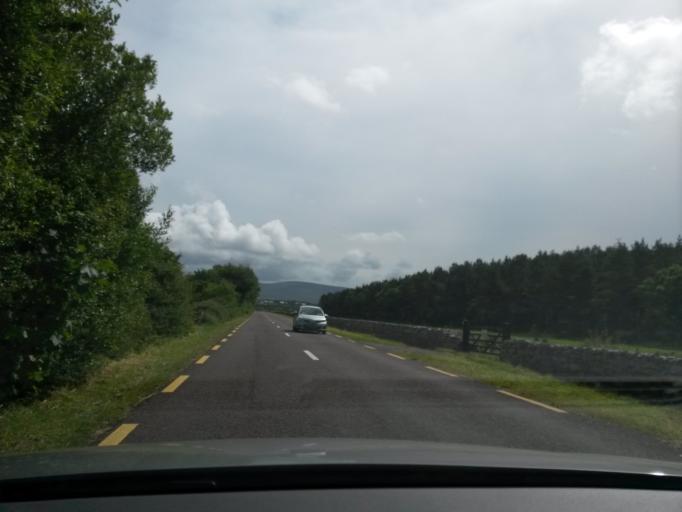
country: IE
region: Connaught
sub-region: County Leitrim
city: Kinlough
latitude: 54.4469
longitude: -8.4545
